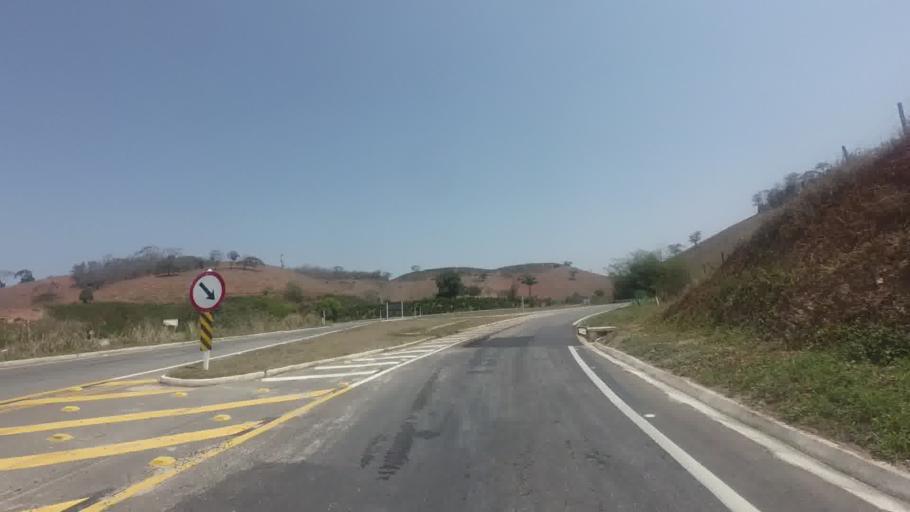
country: BR
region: Espirito Santo
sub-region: Jeronimo Monteiro
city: Jeronimo Monteiro
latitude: -20.8843
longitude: -41.2702
